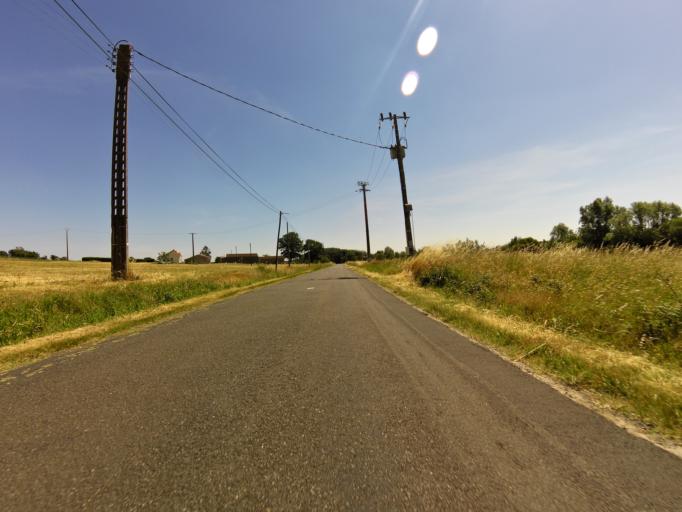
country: FR
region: Pays de la Loire
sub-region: Departement de la Loire-Atlantique
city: Le Loroux-Bottereau
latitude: 47.2059
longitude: -1.3787
